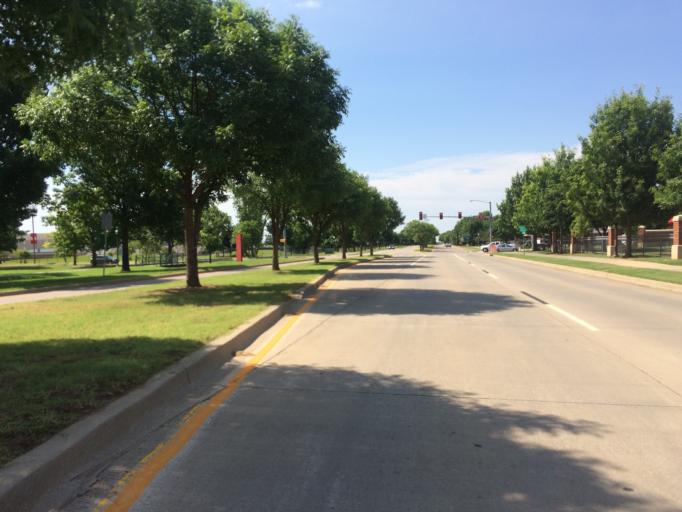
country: US
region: Oklahoma
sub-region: Cleveland County
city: Norman
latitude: 35.1904
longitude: -97.4502
